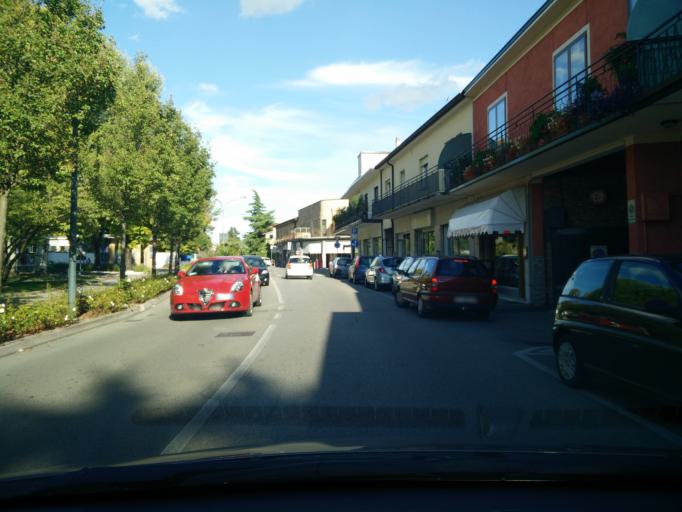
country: IT
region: Veneto
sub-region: Provincia di Venezia
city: San Dona di Piave
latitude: 45.6324
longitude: 12.5724
